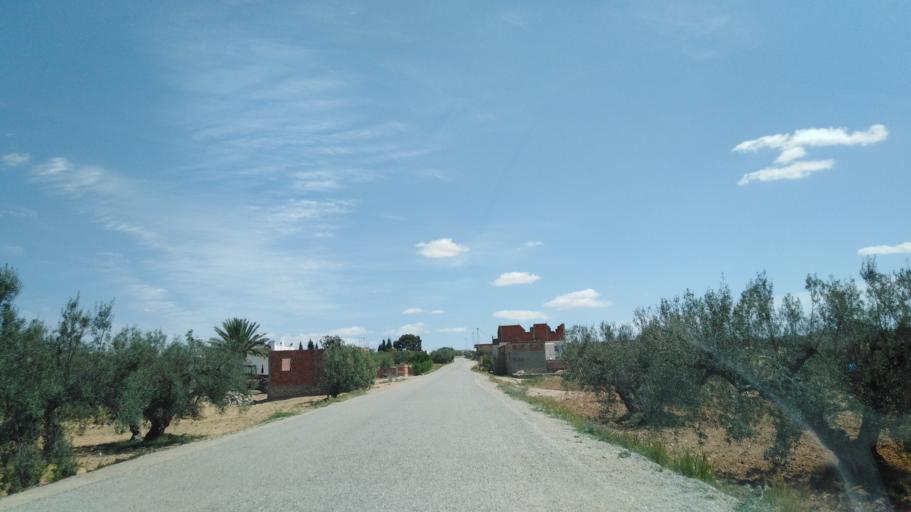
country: TN
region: Safaqis
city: Sfax
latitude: 34.7436
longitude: 10.5475
